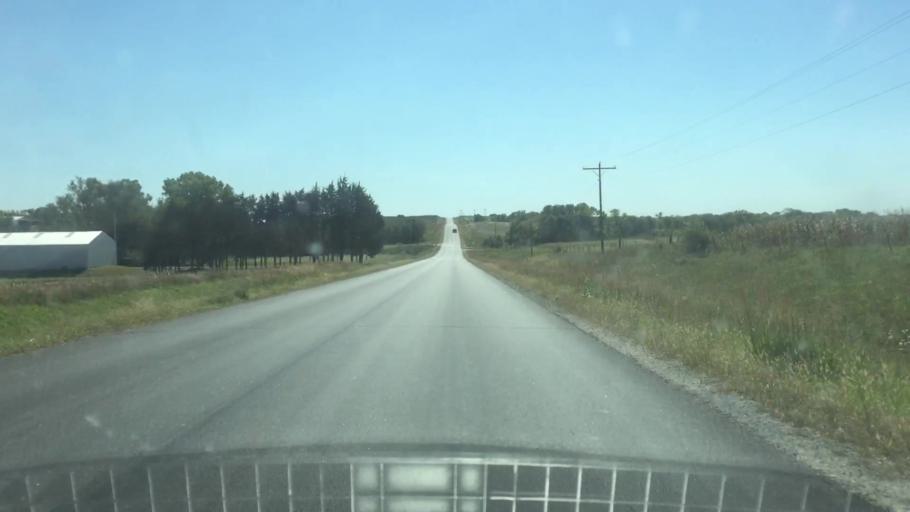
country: US
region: Kansas
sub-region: Marshall County
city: Marysville
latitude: 39.9028
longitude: -96.6010
